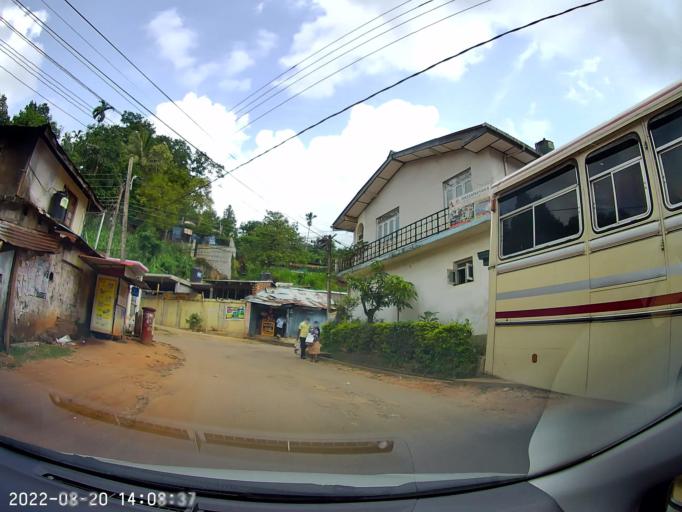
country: LK
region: Central
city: Kandy
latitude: 7.4171
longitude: 80.6831
